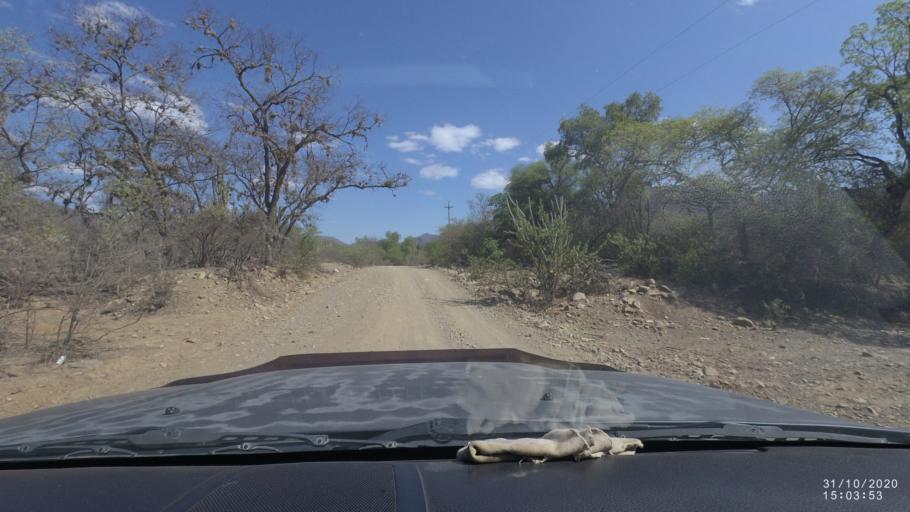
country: BO
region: Cochabamba
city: Aiquile
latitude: -18.2786
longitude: -64.8043
